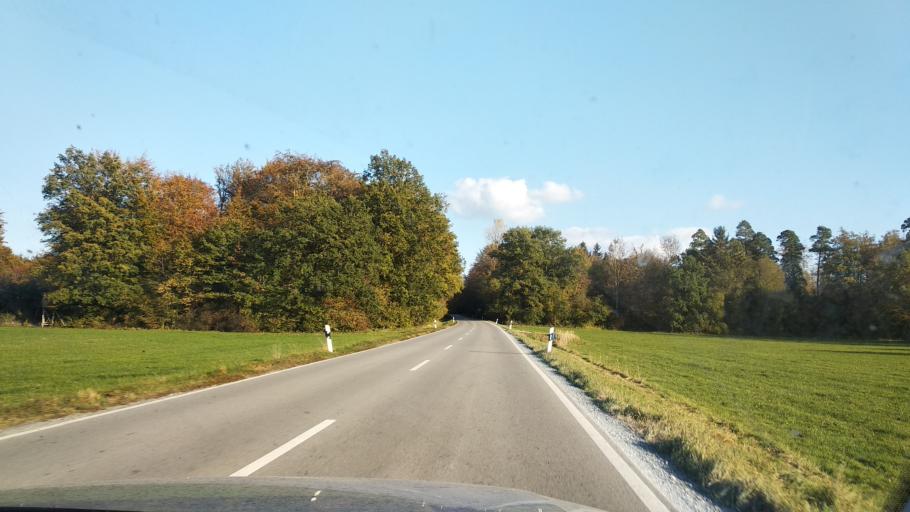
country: DE
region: Bavaria
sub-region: Upper Bavaria
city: Egmating
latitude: 48.0031
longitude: 11.8101
